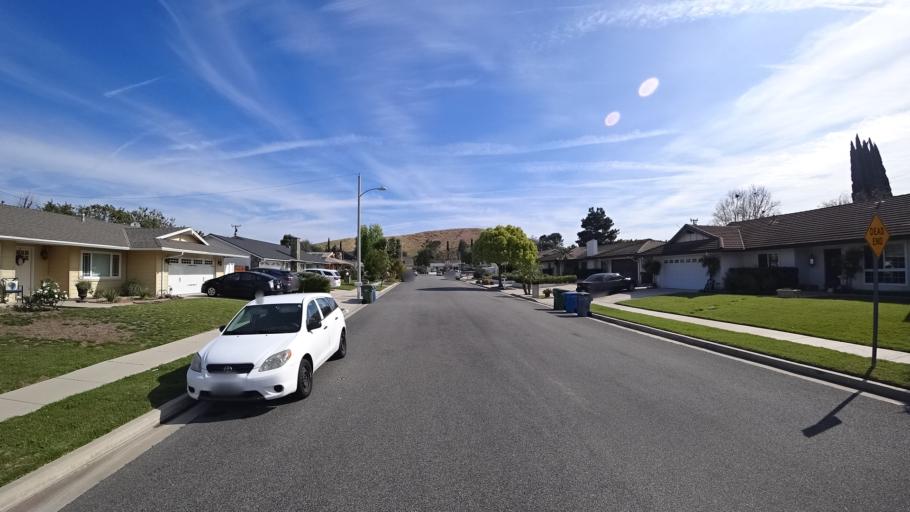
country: US
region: California
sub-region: Ventura County
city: Thousand Oaks
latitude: 34.1987
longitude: -118.8751
